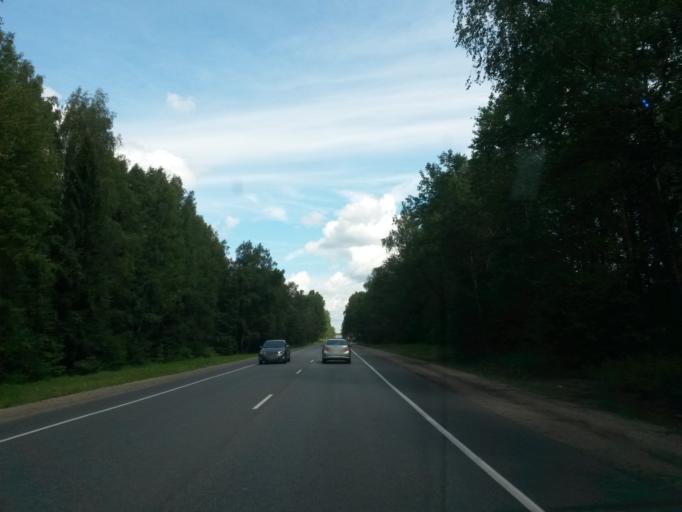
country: RU
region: Jaroslavl
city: Pereslavl'-Zalesskiy
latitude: 56.8132
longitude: 38.9010
